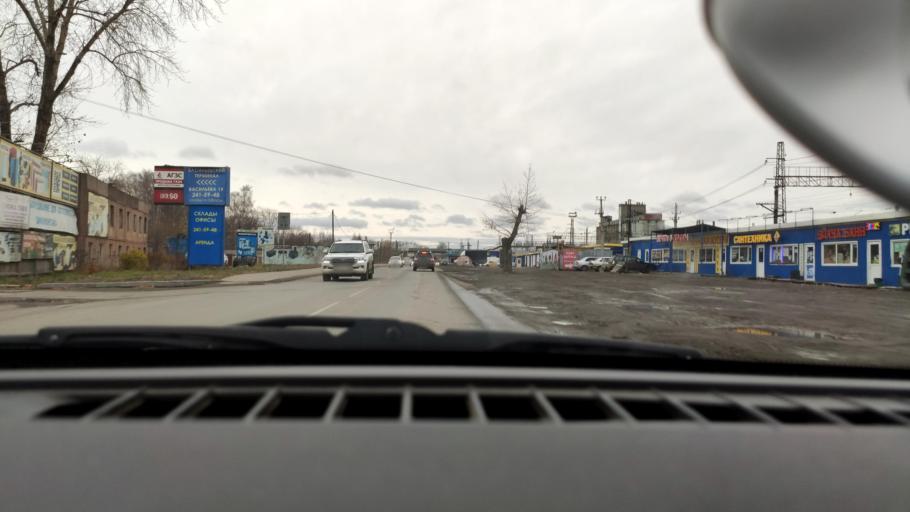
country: RU
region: Perm
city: Froly
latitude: 57.9536
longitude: 56.2306
